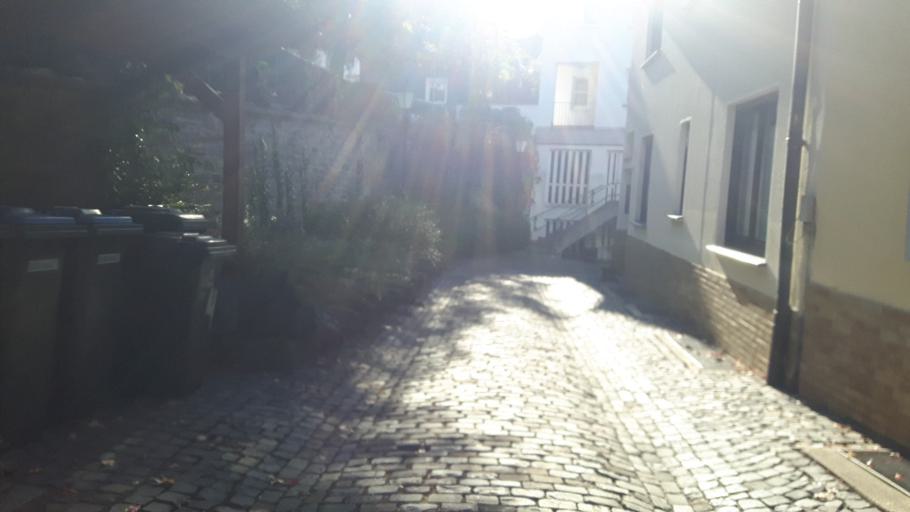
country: DE
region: North Rhine-Westphalia
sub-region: Regierungsbezirk Arnsberg
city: Siegen
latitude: 50.8735
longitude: 8.0267
